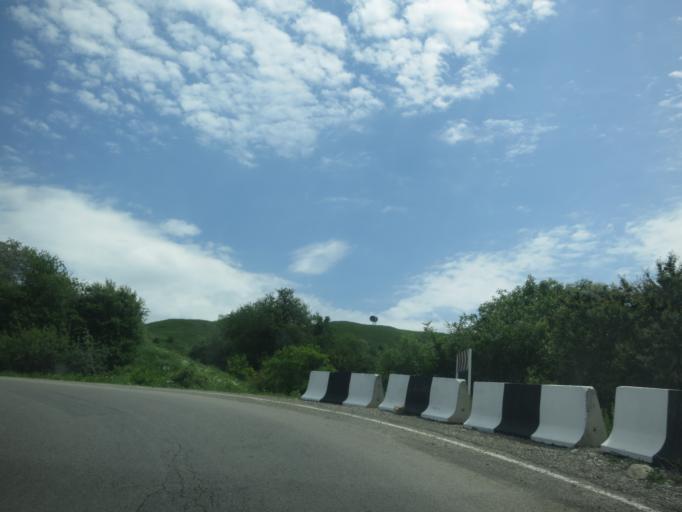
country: GE
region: Kakheti
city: Sagarejo
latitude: 41.8646
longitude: 45.2752
